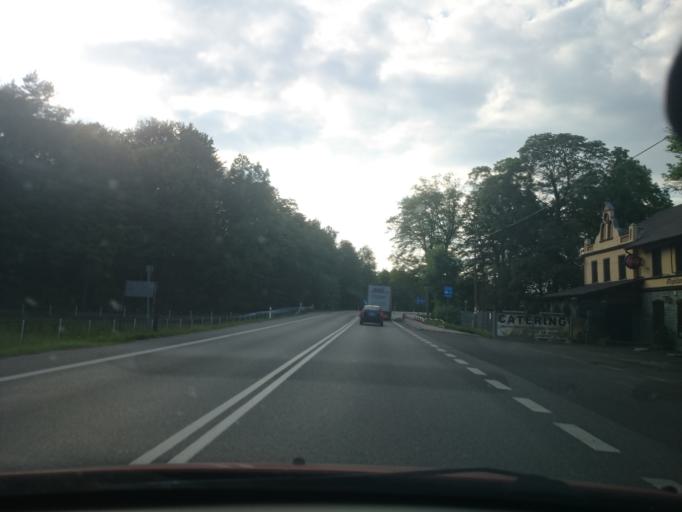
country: PL
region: Opole Voivodeship
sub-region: Powiat opolski
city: Tarnow Opolski
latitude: 50.6040
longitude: 18.0767
